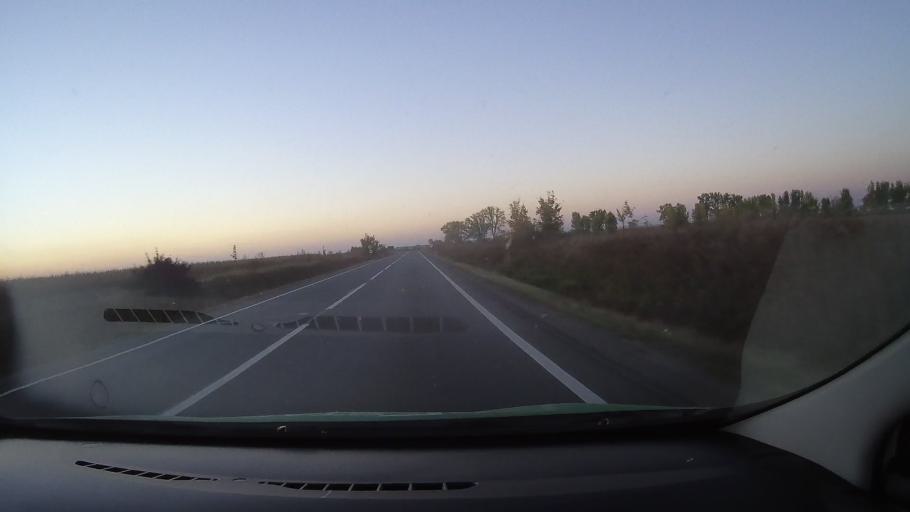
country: RO
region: Bihor
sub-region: Comuna Tarcea
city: Tarcea
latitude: 47.4322
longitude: 22.2059
